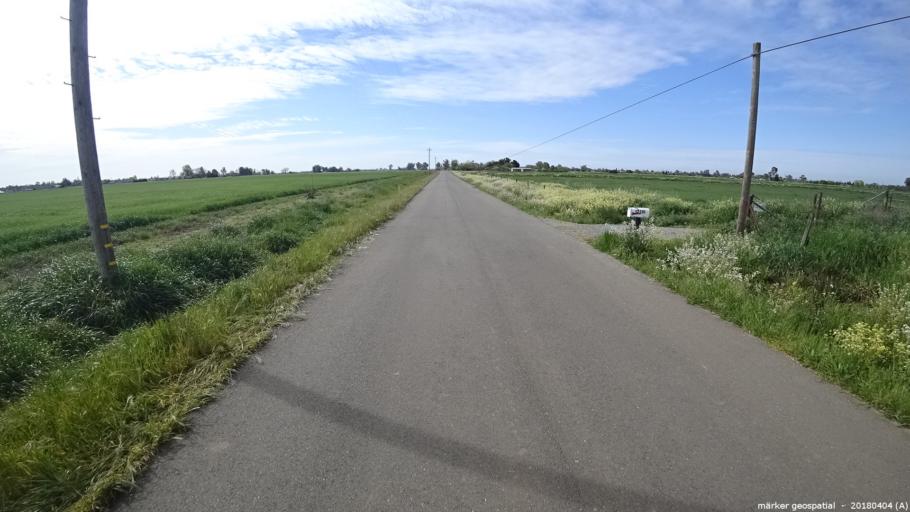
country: US
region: California
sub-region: Sacramento County
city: Herald
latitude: 38.3011
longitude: -121.2772
